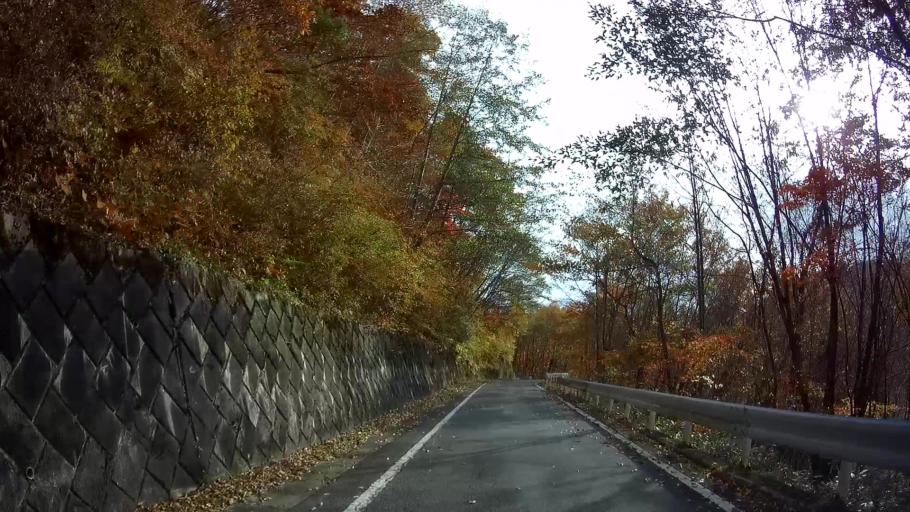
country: JP
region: Gunma
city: Nakanojomachi
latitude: 36.6392
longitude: 138.6439
